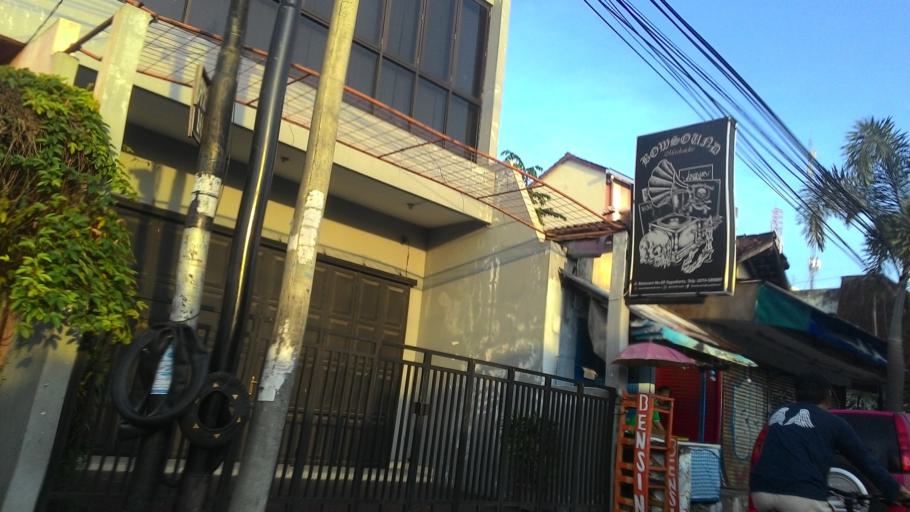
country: ID
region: Daerah Istimewa Yogyakarta
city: Yogyakarta
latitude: -7.7922
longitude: 110.3676
